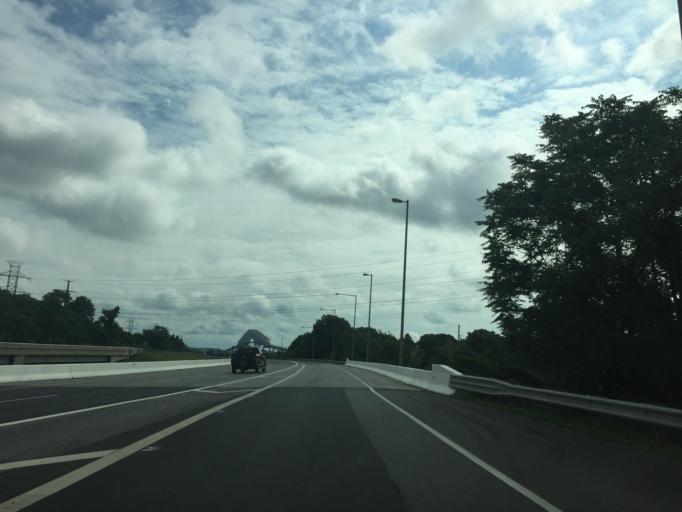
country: US
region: Maryland
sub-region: Baltimore County
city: Dundalk
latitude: 39.2041
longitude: -76.5499
